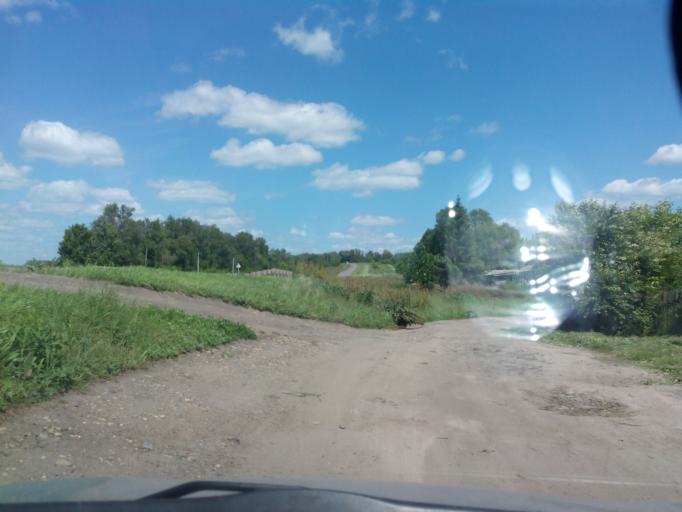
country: RU
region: Tambov
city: Zherdevka
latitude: 51.8393
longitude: 41.5103
